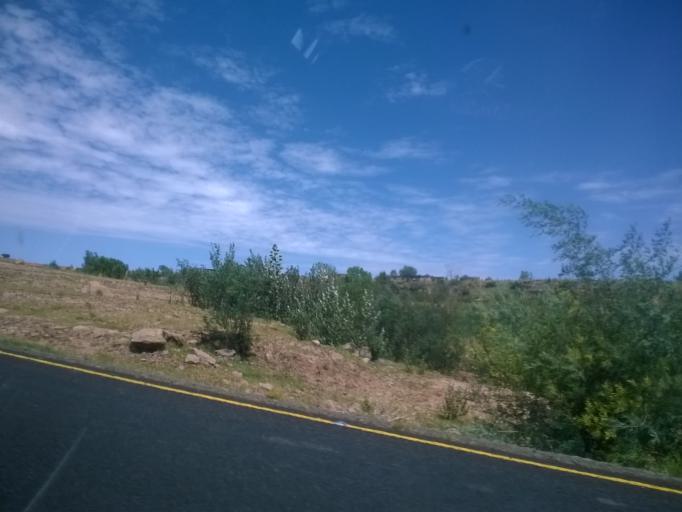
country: LS
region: Berea
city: Teyateyaneng
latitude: -29.0881
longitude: 27.8602
